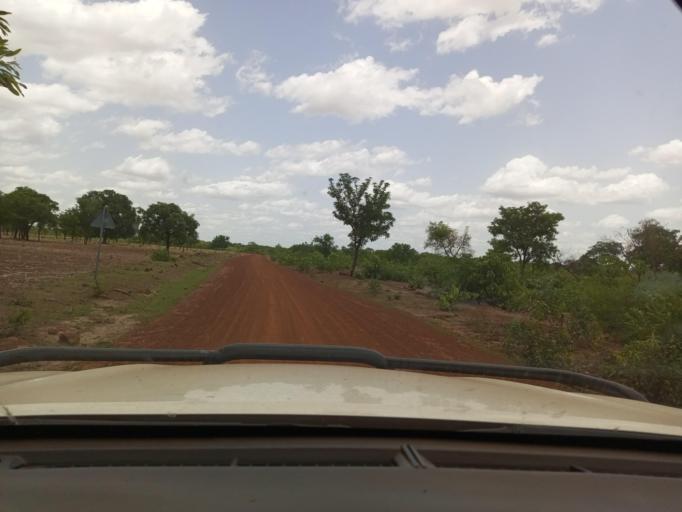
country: ML
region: Sikasso
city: Kolondieba
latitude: 11.7455
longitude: -6.7528
